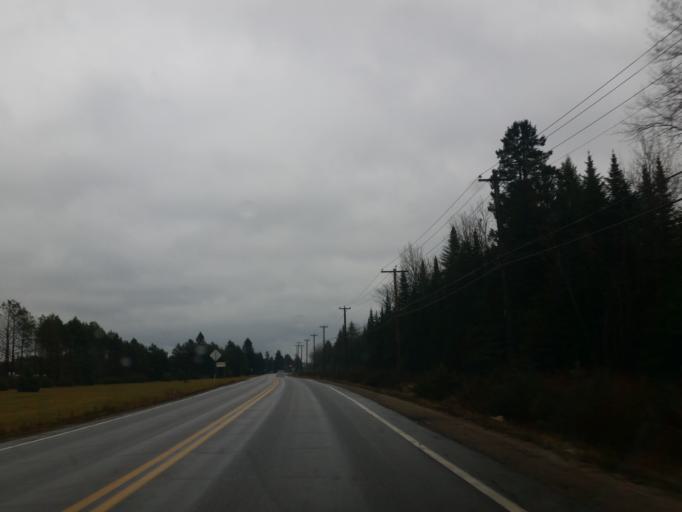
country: CA
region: Quebec
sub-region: Capitale-Nationale
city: Shannon
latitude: 46.8858
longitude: -71.4974
